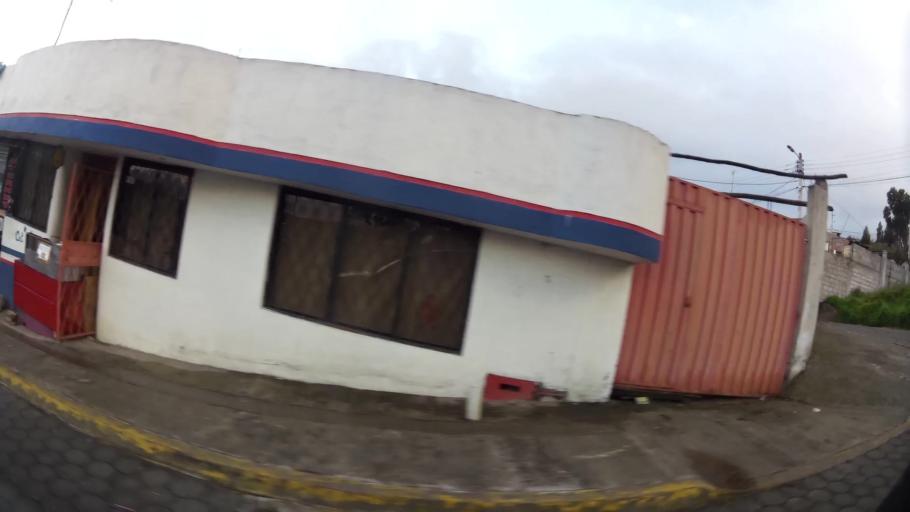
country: EC
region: Pichincha
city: Quito
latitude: -0.1032
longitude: -78.5248
